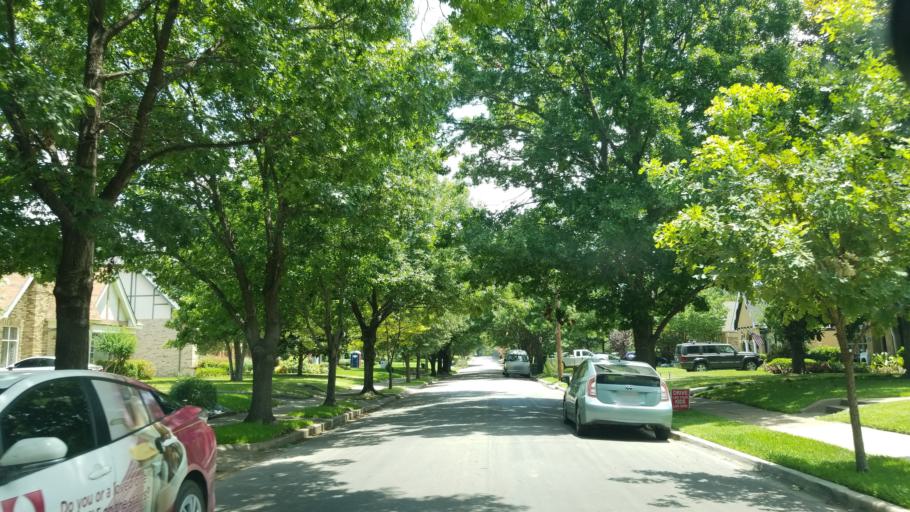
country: US
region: Texas
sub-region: Dallas County
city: Highland Park
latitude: 32.8279
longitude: -96.7650
